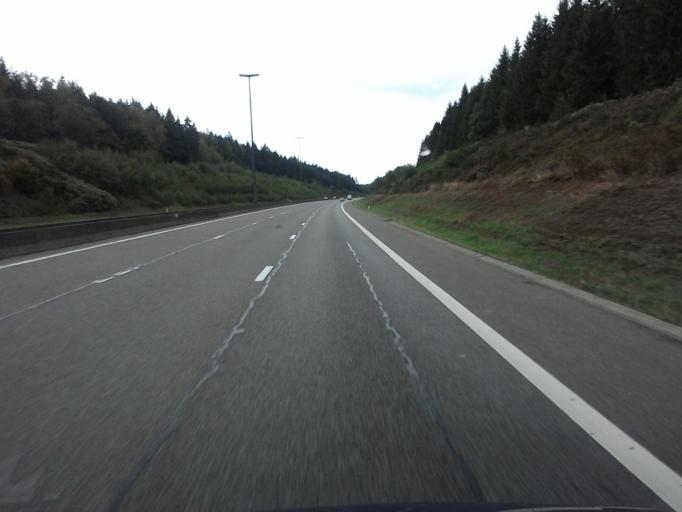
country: BE
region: Wallonia
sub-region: Province du Luxembourg
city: Houffalize
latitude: 50.1850
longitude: 5.7819
